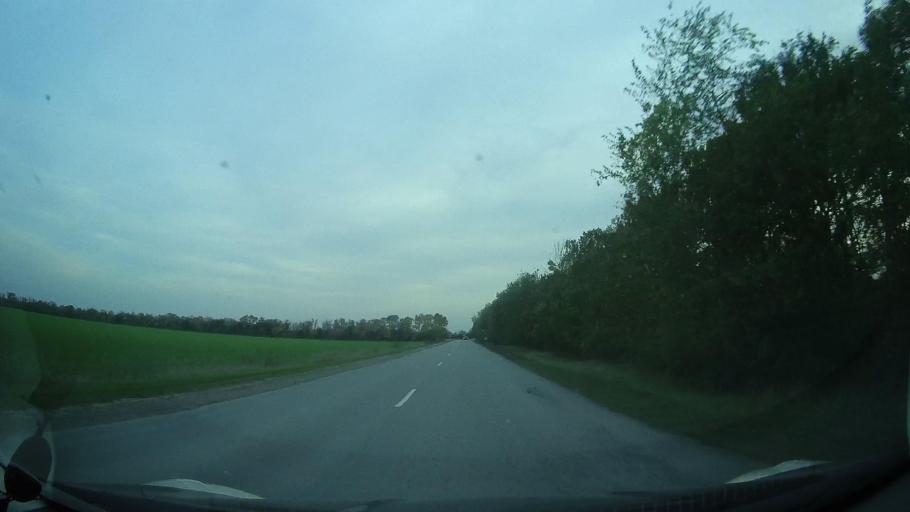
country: RU
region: Rostov
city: Kirovskaya
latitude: 47.0043
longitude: 39.9789
